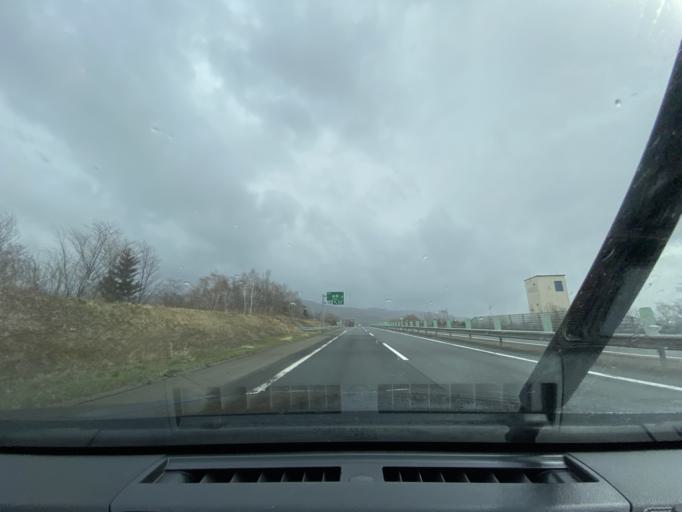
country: JP
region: Hokkaido
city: Bibai
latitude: 43.3368
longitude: 141.8882
